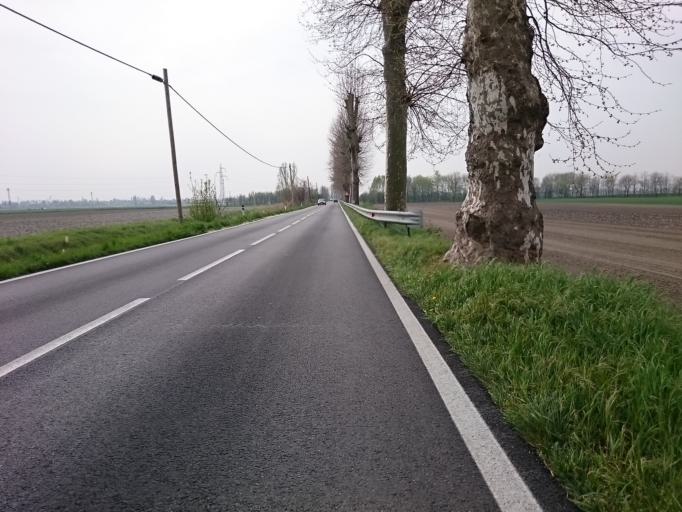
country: IT
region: Veneto
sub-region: Provincia di Padova
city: Anguillara Veneta
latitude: 45.1624
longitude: 11.8774
